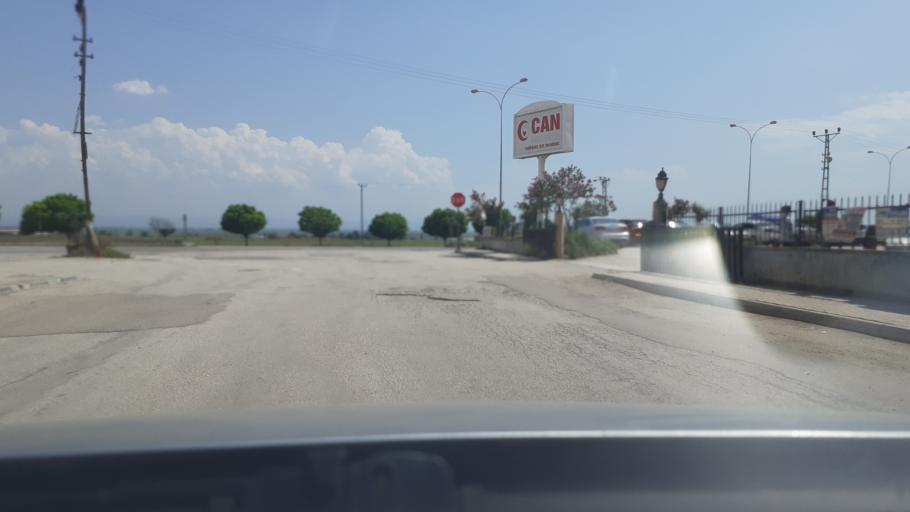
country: TR
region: Hatay
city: Kirikhan
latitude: 36.4802
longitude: 36.3559
